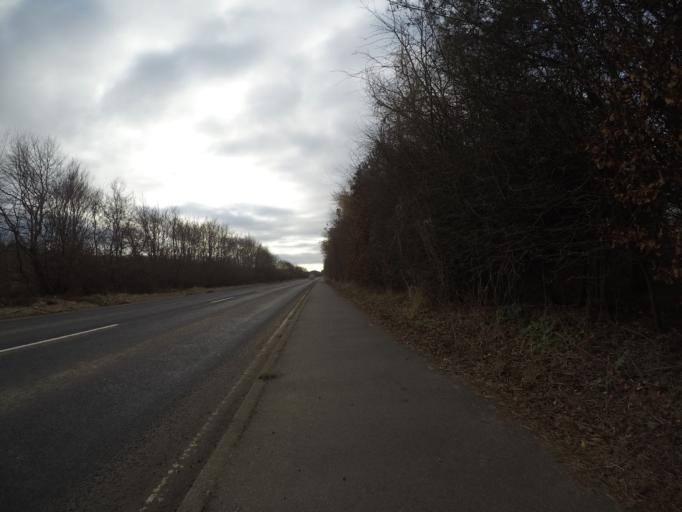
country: GB
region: Scotland
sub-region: North Ayrshire
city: Irvine
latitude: 55.5898
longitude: -4.6504
